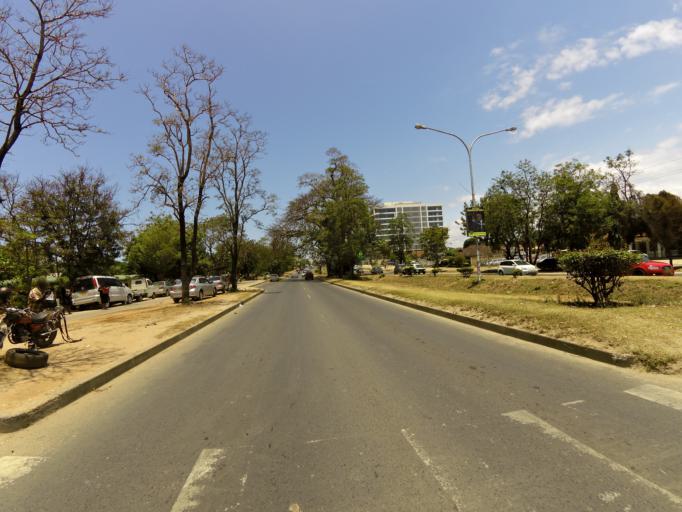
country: TZ
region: Dar es Salaam
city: Magomeni
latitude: -6.7801
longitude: 39.2730
